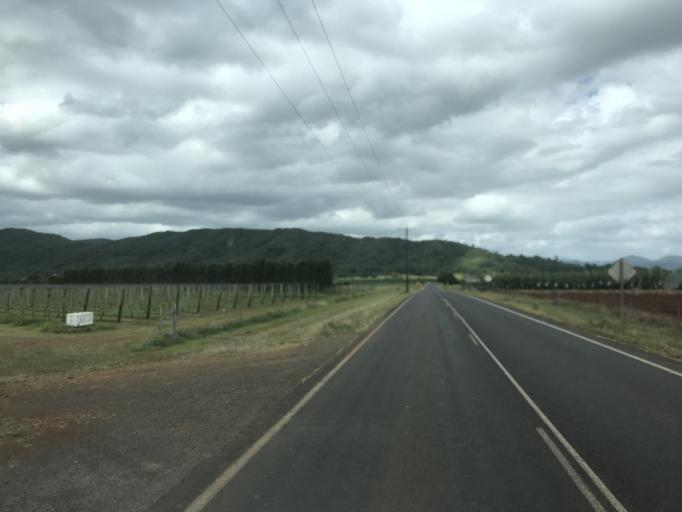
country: AU
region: Queensland
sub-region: Cassowary Coast
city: Innisfail
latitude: -17.6057
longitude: 146.0112
